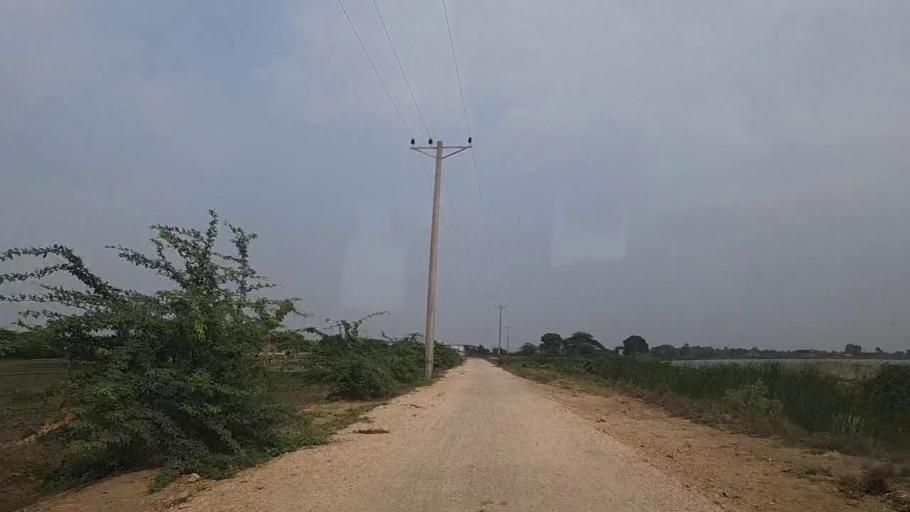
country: PK
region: Sindh
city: Mirpur Sakro
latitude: 24.6059
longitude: 67.7025
